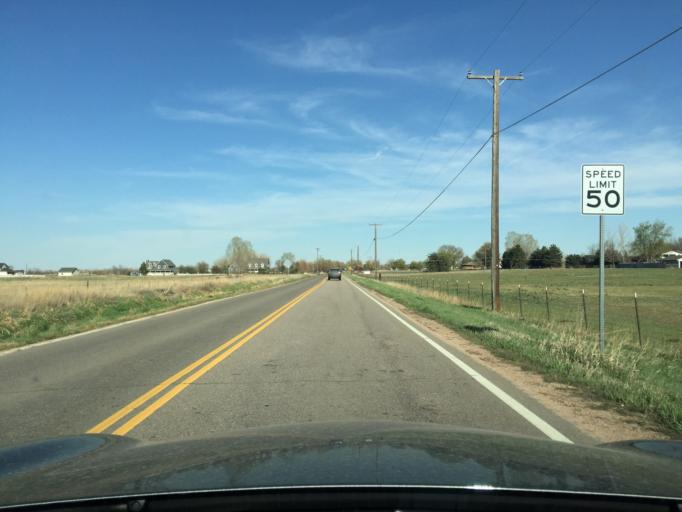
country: US
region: Colorado
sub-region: Boulder County
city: Erie
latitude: 40.0545
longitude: -105.1016
